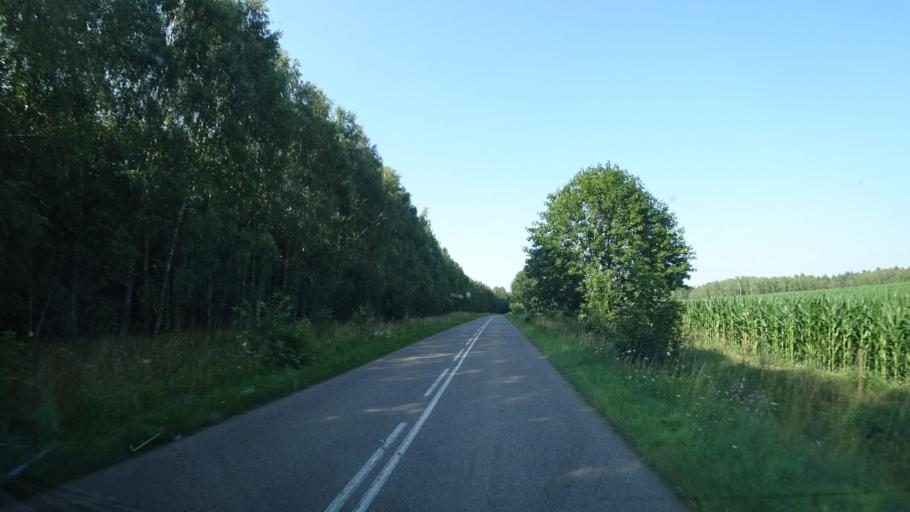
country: PL
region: Pomeranian Voivodeship
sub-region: Powiat czluchowski
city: Rzeczenica
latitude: 53.7846
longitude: 17.1672
